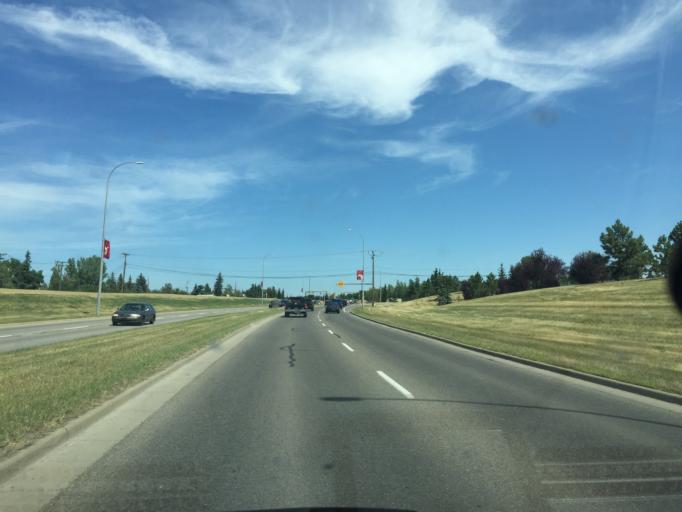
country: CA
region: Alberta
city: Calgary
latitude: 50.9387
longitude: -114.0317
